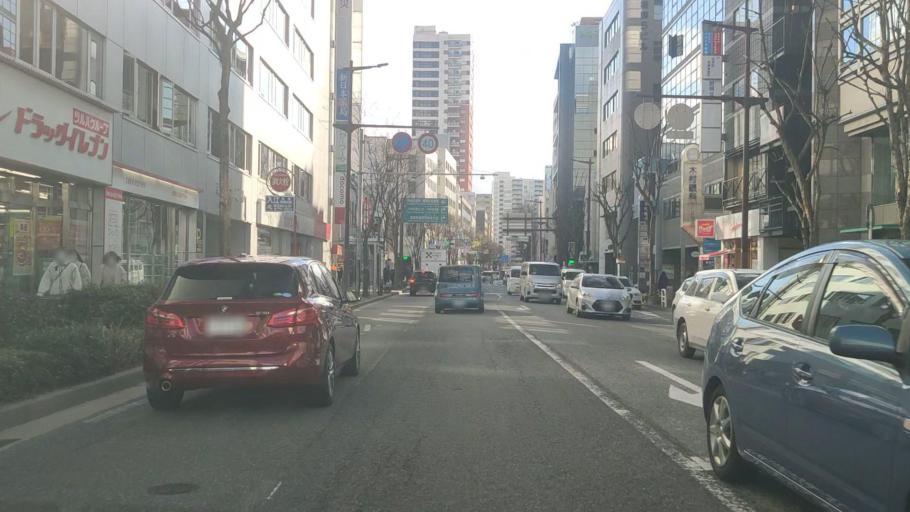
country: JP
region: Fukuoka
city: Fukuoka-shi
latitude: 33.5890
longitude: 130.3906
